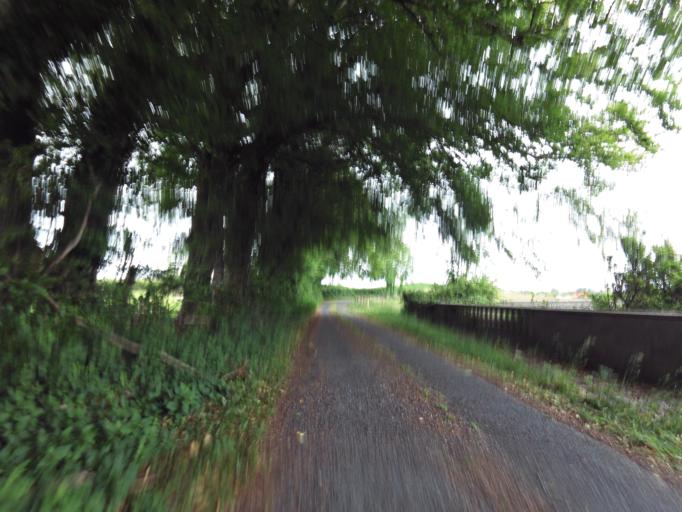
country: IE
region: Connaught
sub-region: County Galway
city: Athenry
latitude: 53.3143
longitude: -8.7305
